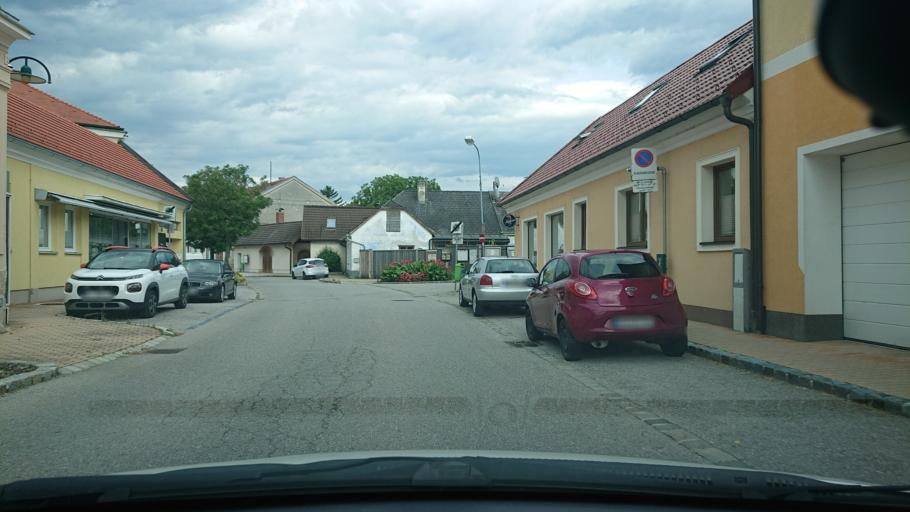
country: AT
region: Lower Austria
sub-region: Politischer Bezirk Baden
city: Hirtenberg
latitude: 47.9376
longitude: 16.1517
